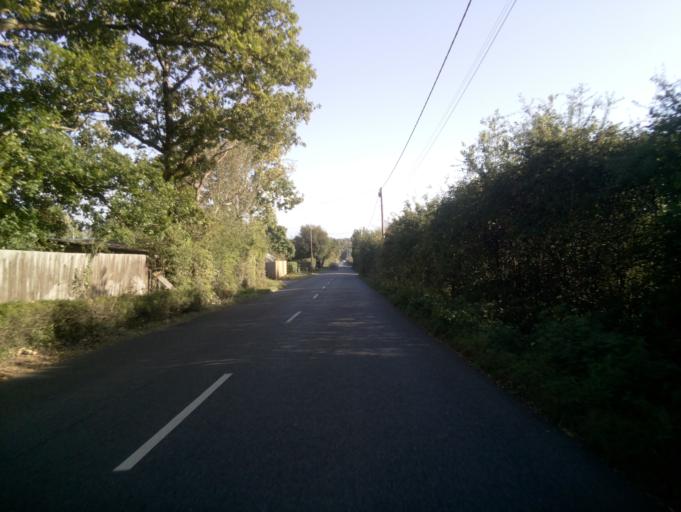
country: GB
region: England
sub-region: Hampshire
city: Swanmore
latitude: 50.9294
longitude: -1.1692
